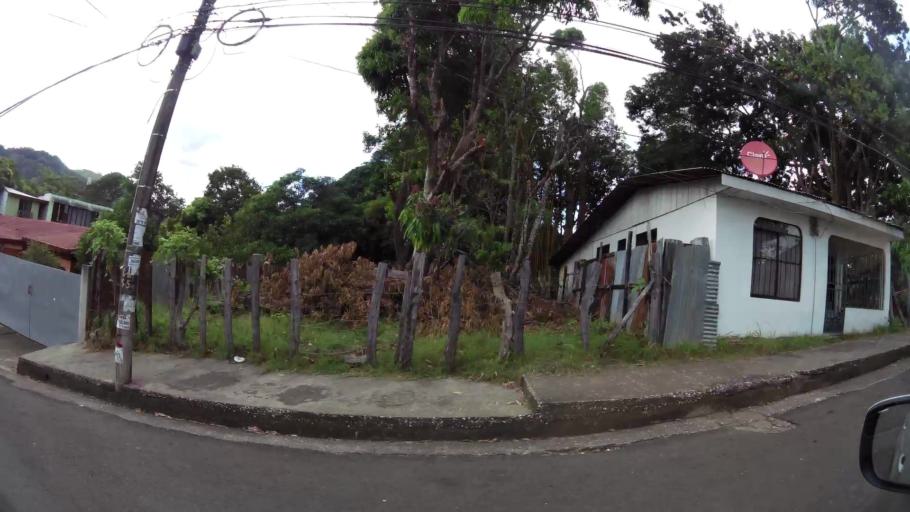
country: CR
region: Guanacaste
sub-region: Canton de Nicoya
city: Nicoya
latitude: 10.1415
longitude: -85.4539
